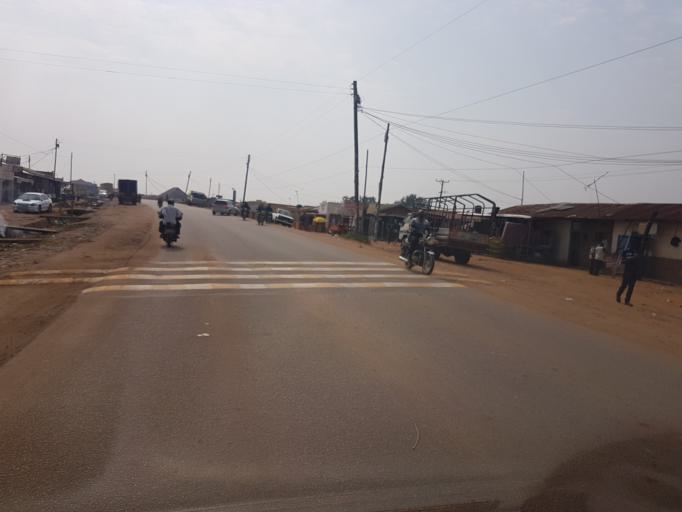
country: UG
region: Western Region
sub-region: Mbarara District
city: Mbarara
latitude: -0.6344
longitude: 30.6190
